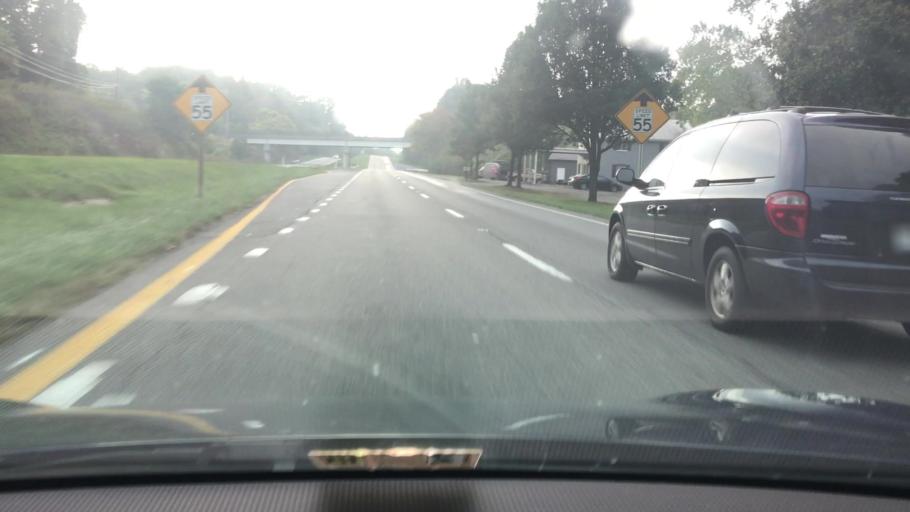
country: US
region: Virginia
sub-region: Botetourt County
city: Blue Ridge
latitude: 37.3958
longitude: -79.7490
